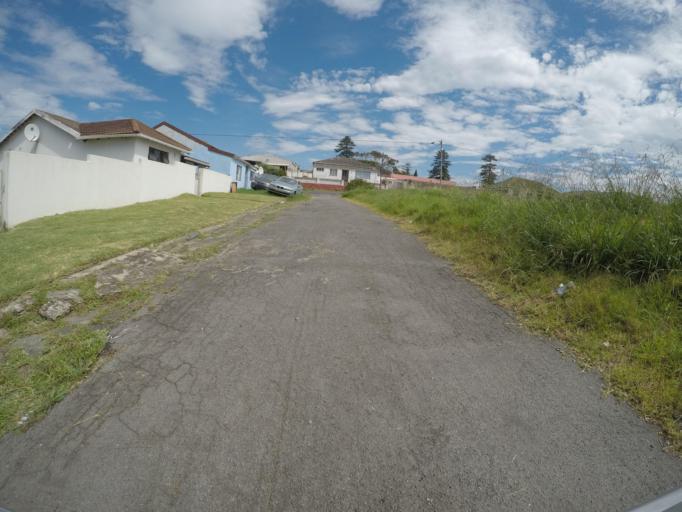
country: ZA
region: Eastern Cape
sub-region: Buffalo City Metropolitan Municipality
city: East London
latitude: -33.0326
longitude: 27.9104
